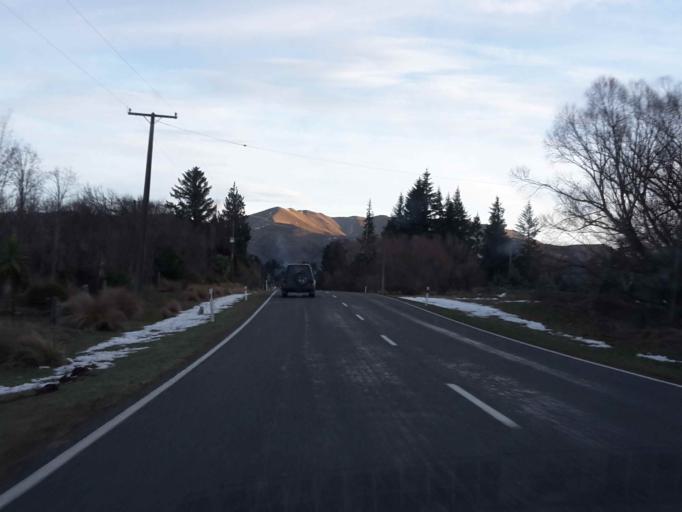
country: NZ
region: Canterbury
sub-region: Timaru District
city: Pleasant Point
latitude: -44.0829
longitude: 170.6601
